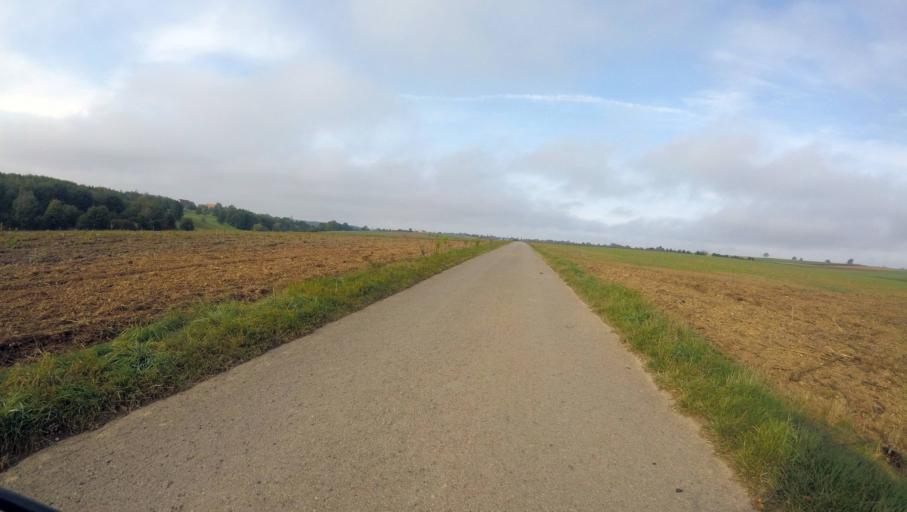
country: DE
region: Baden-Wuerttemberg
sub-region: Regierungsbezirk Stuttgart
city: Motzingen
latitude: 48.5339
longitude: 8.8029
